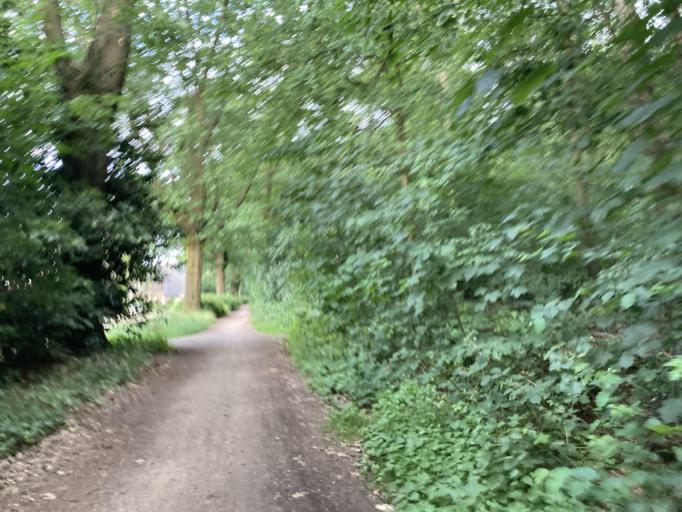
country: NL
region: North Brabant
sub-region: Gemeente Eindhoven
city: Eindhoven
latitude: 51.4784
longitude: 5.4497
